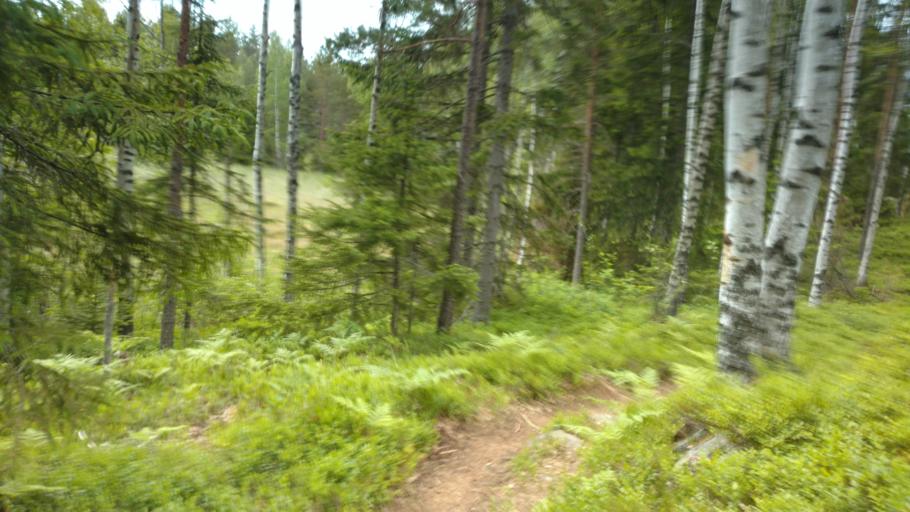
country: FI
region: Uusimaa
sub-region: Raaseporin
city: Pohja
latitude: 60.1128
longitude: 23.5522
